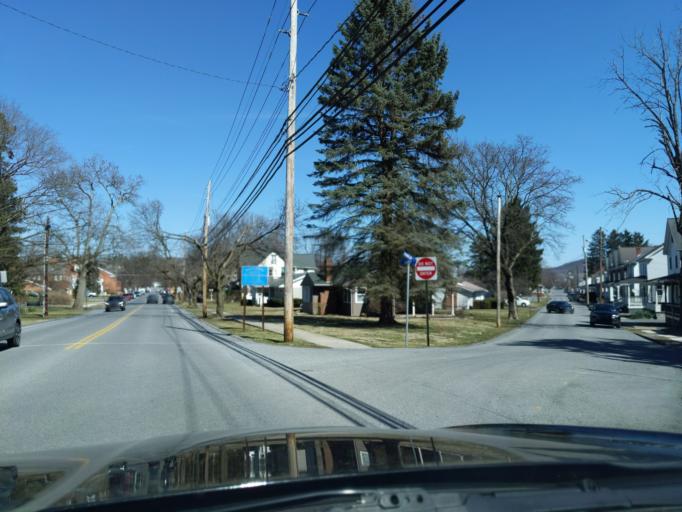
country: US
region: Pennsylvania
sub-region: Blair County
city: Hollidaysburg
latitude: 40.4236
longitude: -78.3999
